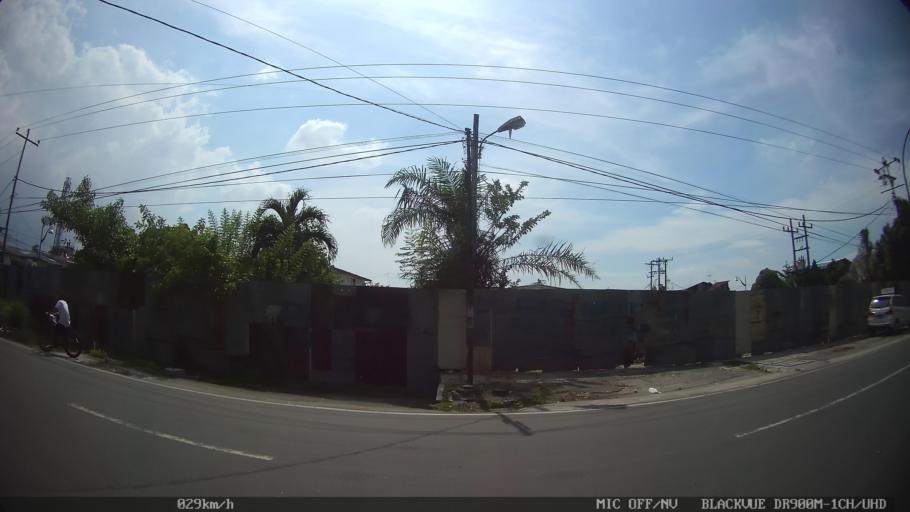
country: ID
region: North Sumatra
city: Medan
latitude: 3.6010
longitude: 98.6691
